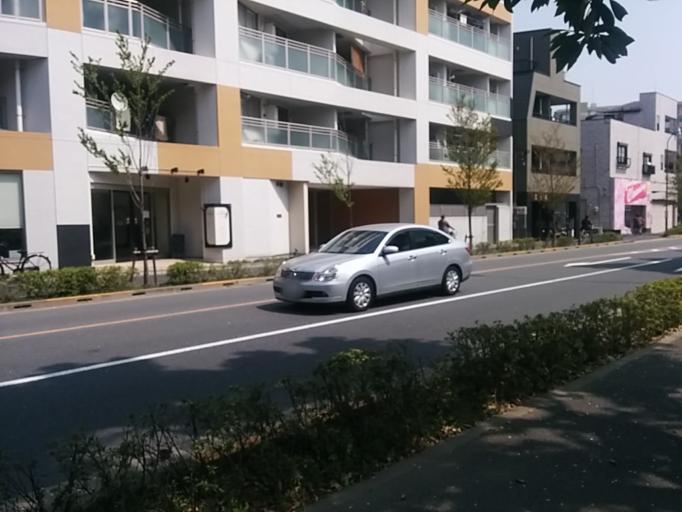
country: JP
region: Tokyo
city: Urayasu
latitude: 35.6810
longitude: 139.8683
